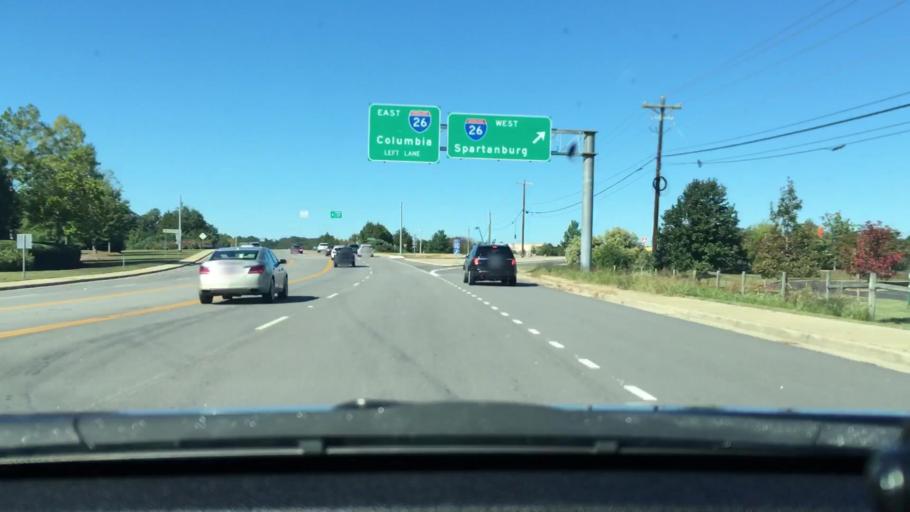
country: US
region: South Carolina
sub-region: Lexington County
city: Irmo
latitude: 34.0907
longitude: -81.1630
